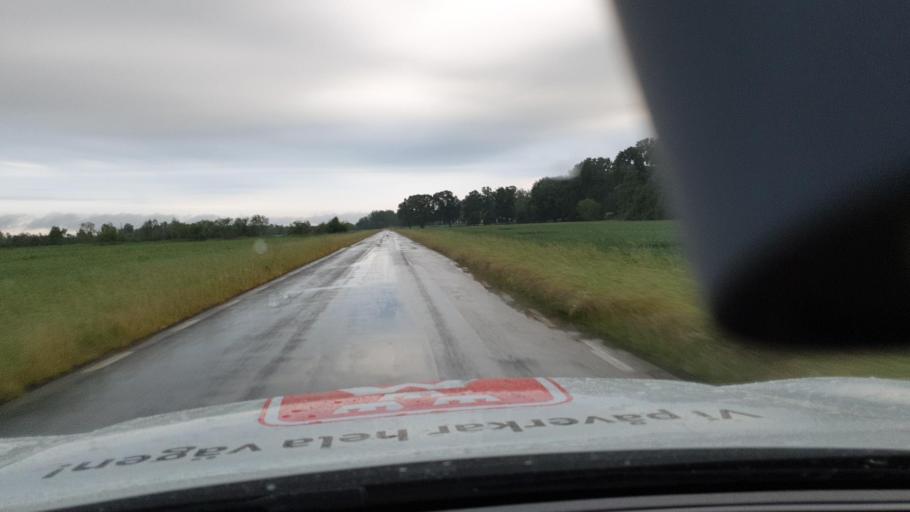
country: SE
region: Vaestra Goetaland
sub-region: Skovde Kommun
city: Stopen
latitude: 58.5153
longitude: 13.8701
